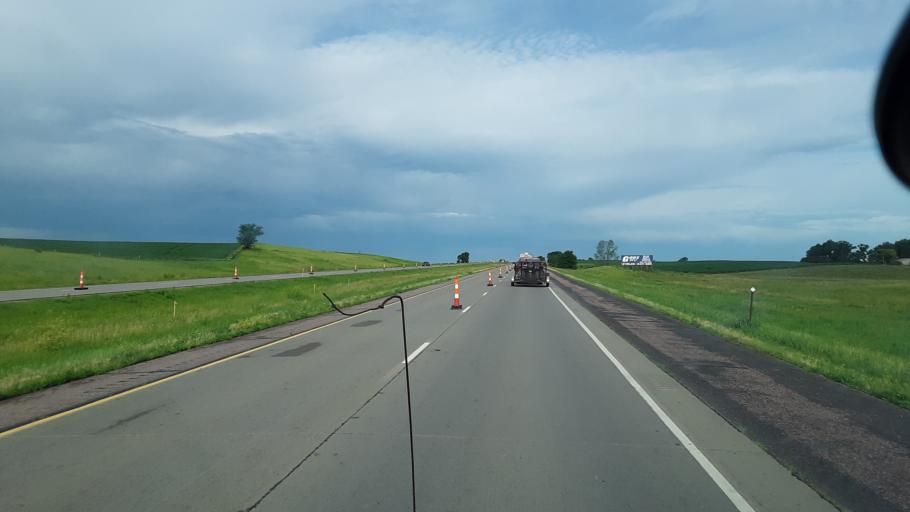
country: US
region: South Dakota
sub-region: Minnehaha County
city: Crooks
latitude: 43.6087
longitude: -96.8436
